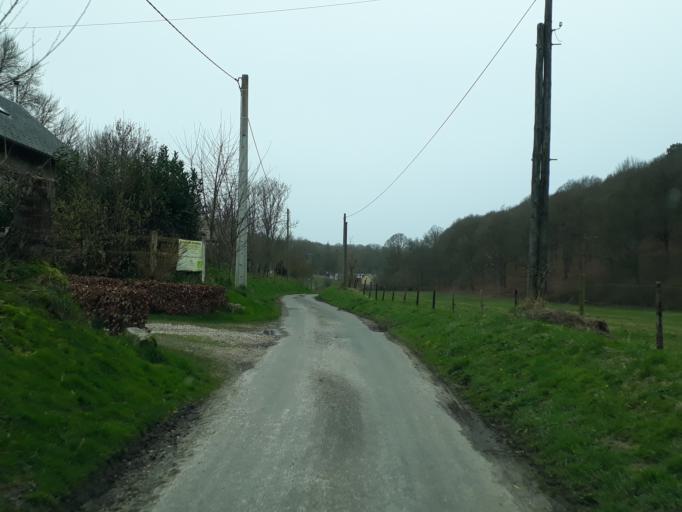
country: FR
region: Haute-Normandie
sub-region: Departement de la Seine-Maritime
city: Les Loges
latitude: 49.6699
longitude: 0.2777
